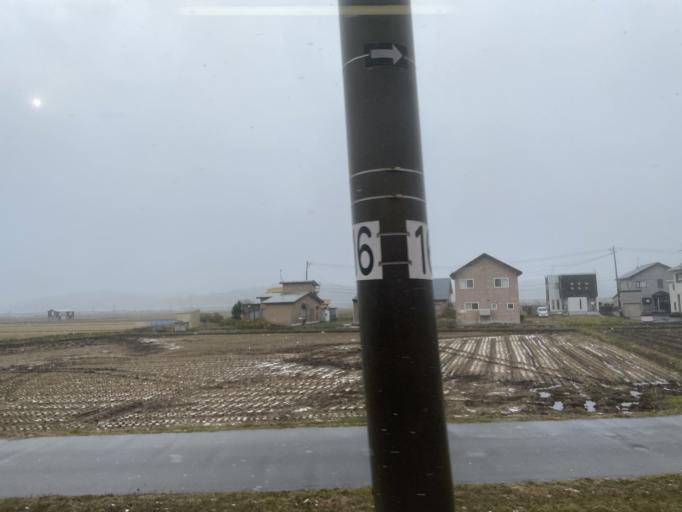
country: JP
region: Aomori
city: Aomori Shi
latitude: 40.9126
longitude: 140.6689
